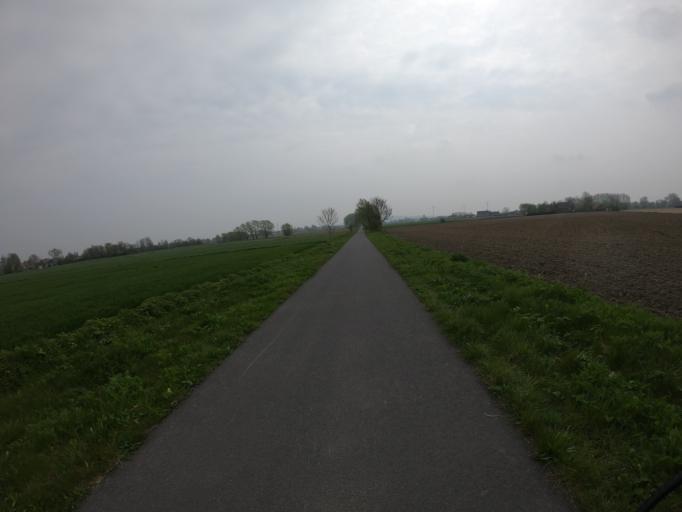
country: BE
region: Flanders
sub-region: Provincie West-Vlaanderen
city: Avelgem
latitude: 50.7757
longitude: 3.4173
